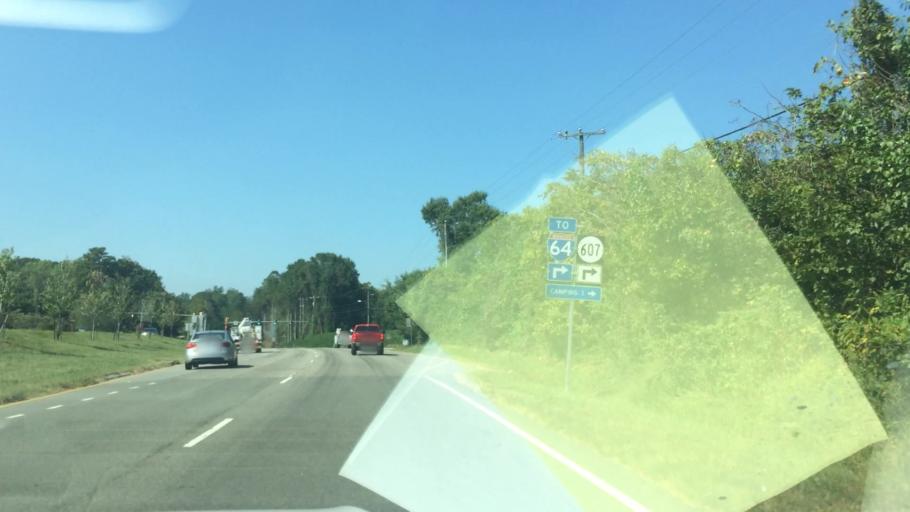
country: US
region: Virginia
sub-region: James City County
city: Williamsburg
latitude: 37.3724
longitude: -76.7761
